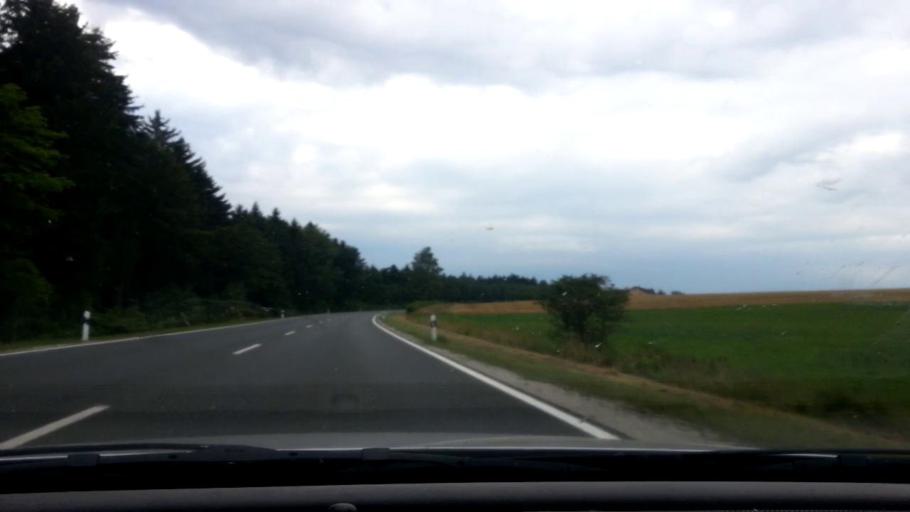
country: DE
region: Bavaria
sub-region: Upper Palatinate
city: Erbendorf
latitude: 49.8387
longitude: 12.0096
